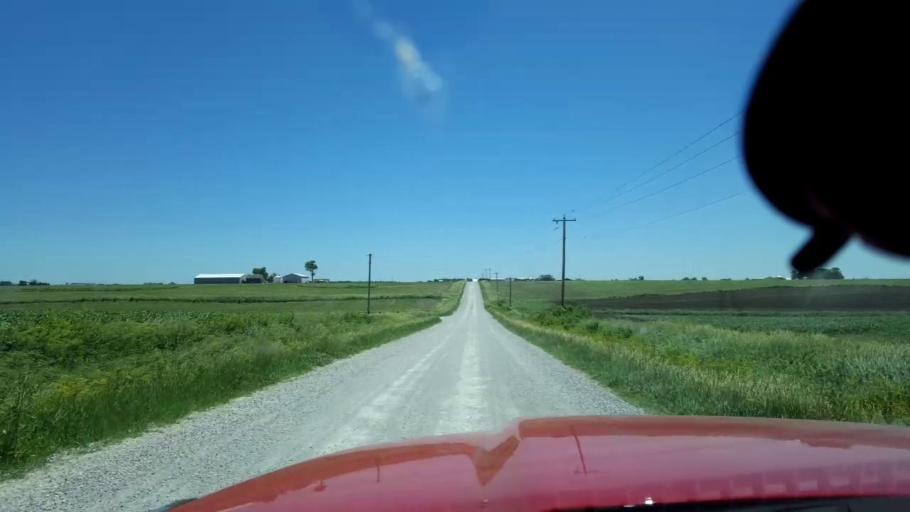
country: US
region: Iowa
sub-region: Washington County
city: Washington
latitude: 41.2799
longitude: -91.6522
